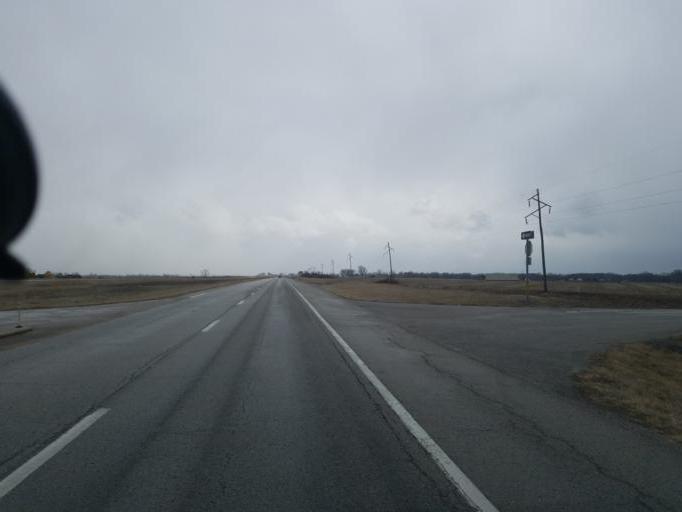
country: US
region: Missouri
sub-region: Randolph County
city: Moberly
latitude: 39.5417
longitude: -92.4502
